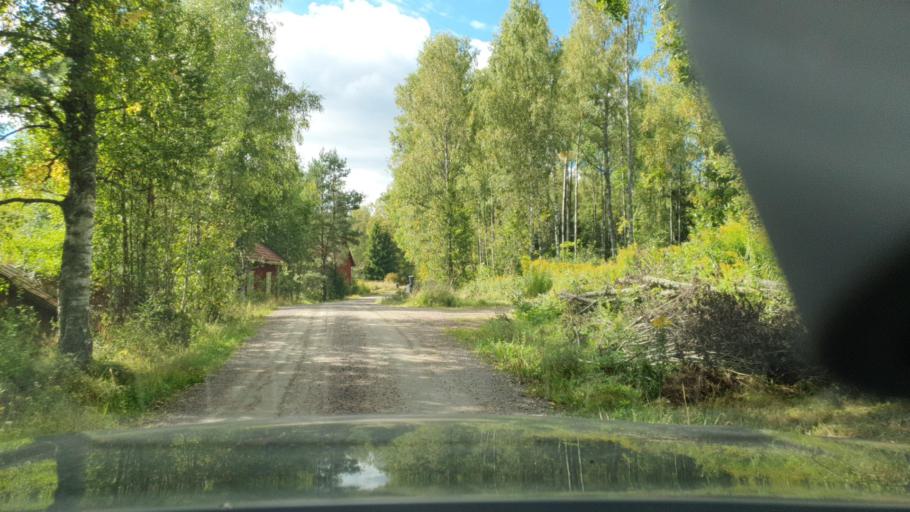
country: SE
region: Vaermland
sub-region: Karlstads Kommun
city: Molkom
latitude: 59.5588
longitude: 13.7500
